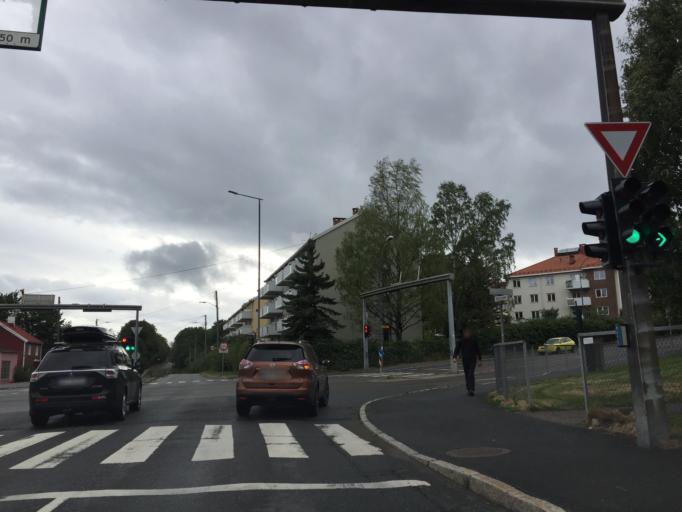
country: NO
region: Oslo
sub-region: Oslo
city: Oslo
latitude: 59.9242
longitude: 10.7919
